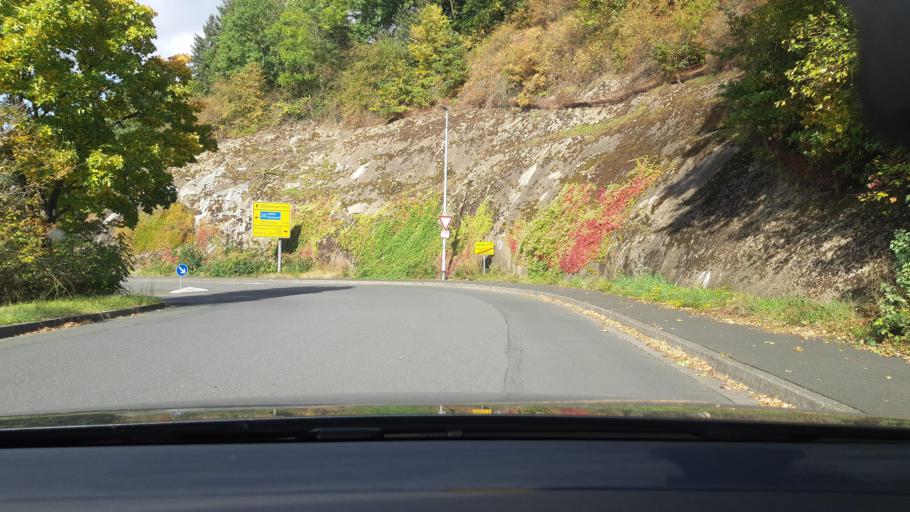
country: DE
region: Hesse
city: Herborn
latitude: 50.6782
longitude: 8.3106
